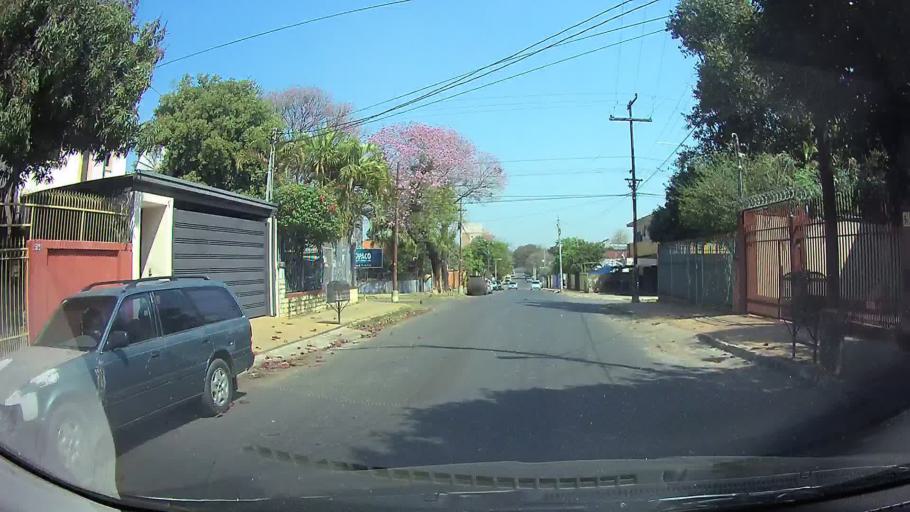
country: PY
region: Asuncion
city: Asuncion
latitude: -25.2962
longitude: -57.6418
